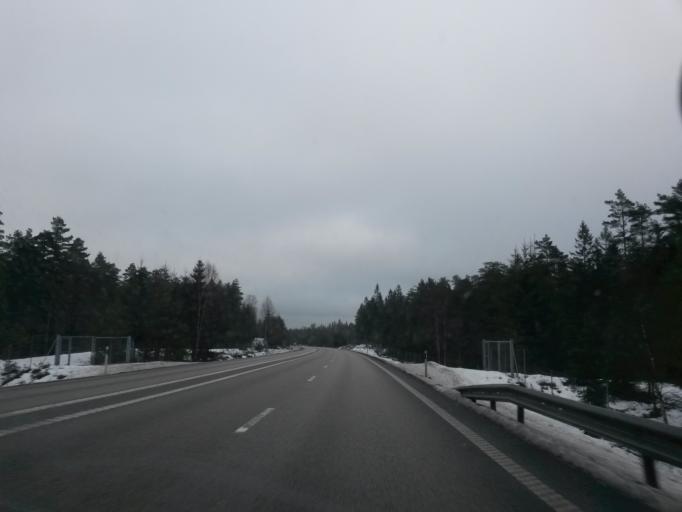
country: SE
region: Vaestra Goetaland
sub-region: Marks Kommun
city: Fritsla
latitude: 57.5474
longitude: 12.8203
